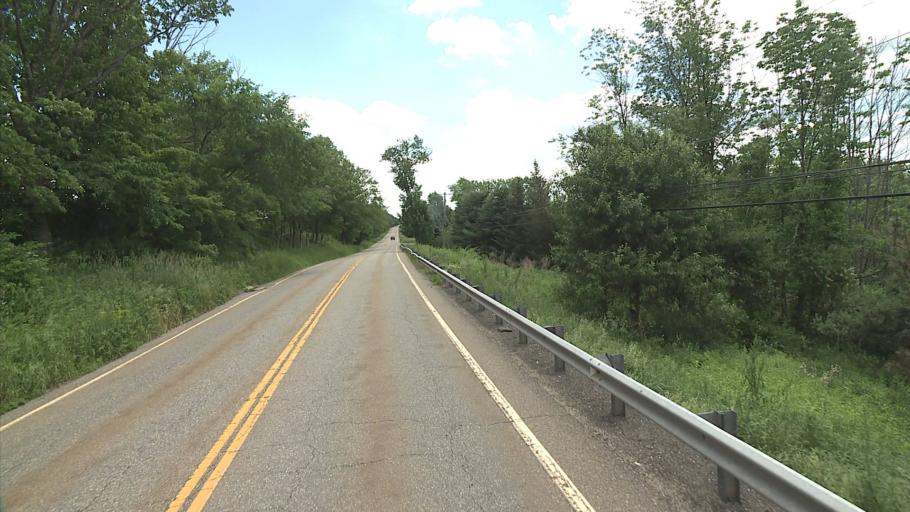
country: US
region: Connecticut
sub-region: Litchfield County
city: Litchfield
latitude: 41.8141
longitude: -73.2188
